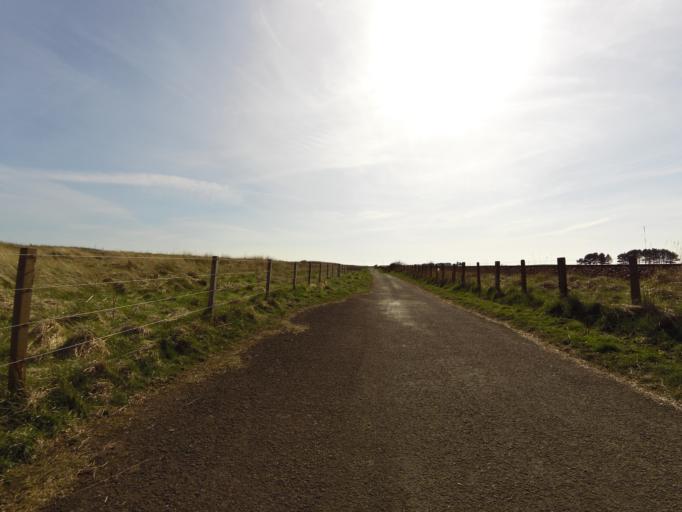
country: GB
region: Scotland
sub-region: Angus
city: Arbroath
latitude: 56.5384
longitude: -2.6264
